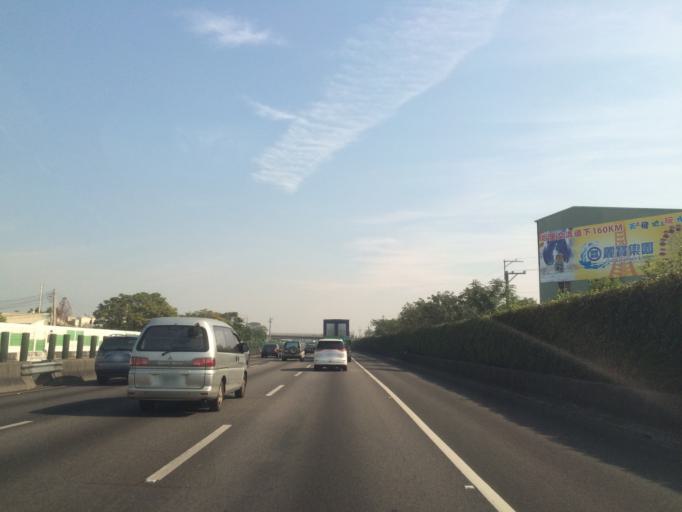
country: TW
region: Taiwan
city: Fengyuan
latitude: 24.2107
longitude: 120.6677
